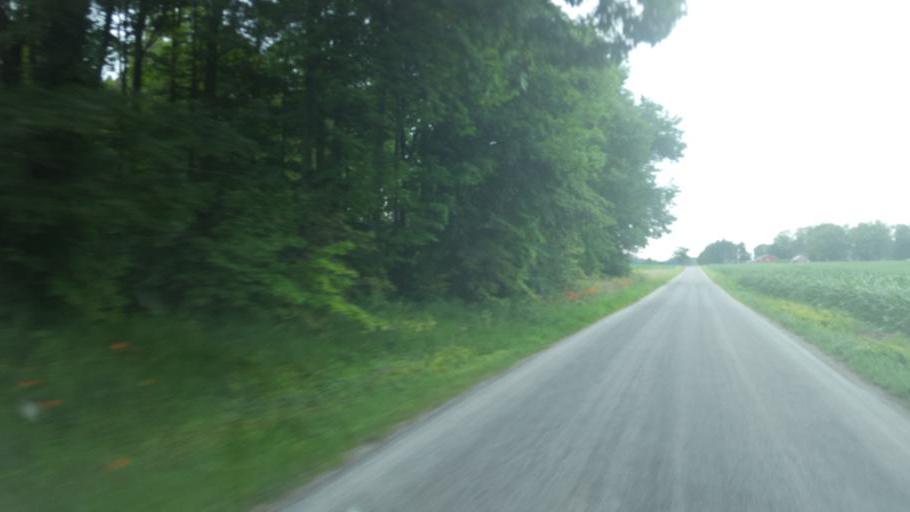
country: US
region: Ohio
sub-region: Huron County
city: Greenwich
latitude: 40.9272
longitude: -82.4748
